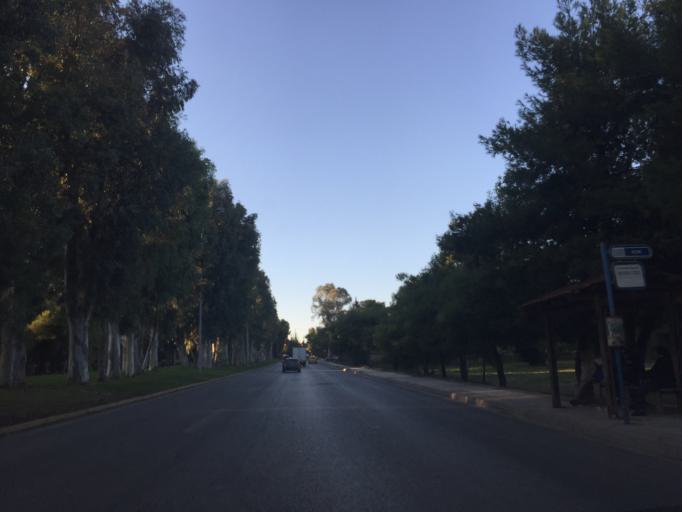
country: GR
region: Attica
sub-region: Nomarchia Anatolikis Attikis
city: Vouliagmeni
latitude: 37.8190
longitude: 23.7770
